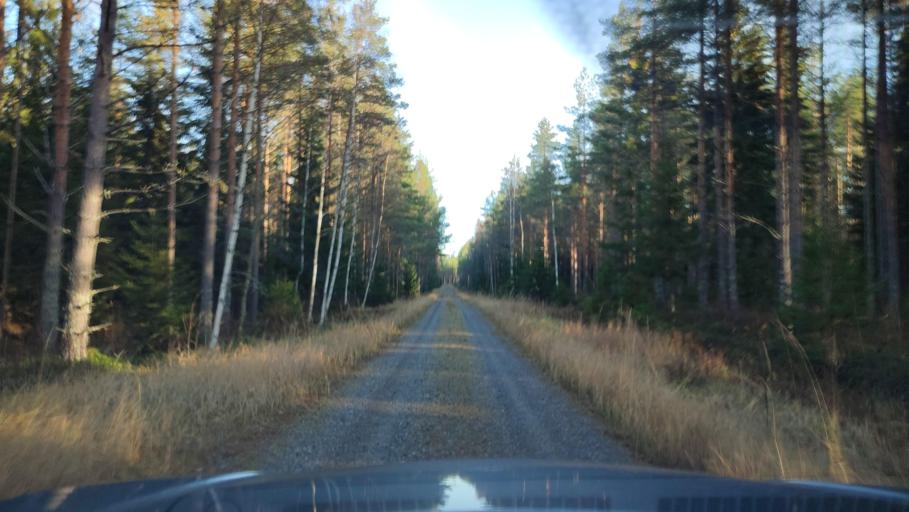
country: FI
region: Southern Ostrobothnia
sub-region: Suupohja
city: Karijoki
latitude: 62.1956
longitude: 21.6082
